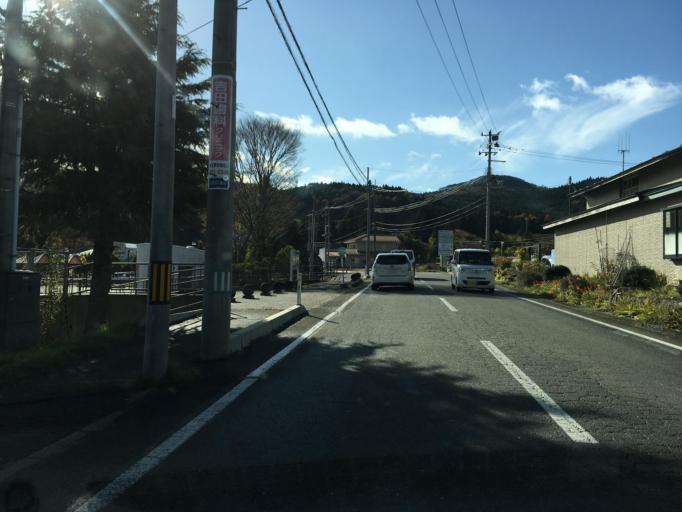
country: JP
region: Iwate
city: Ofunato
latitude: 38.9365
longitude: 141.4438
